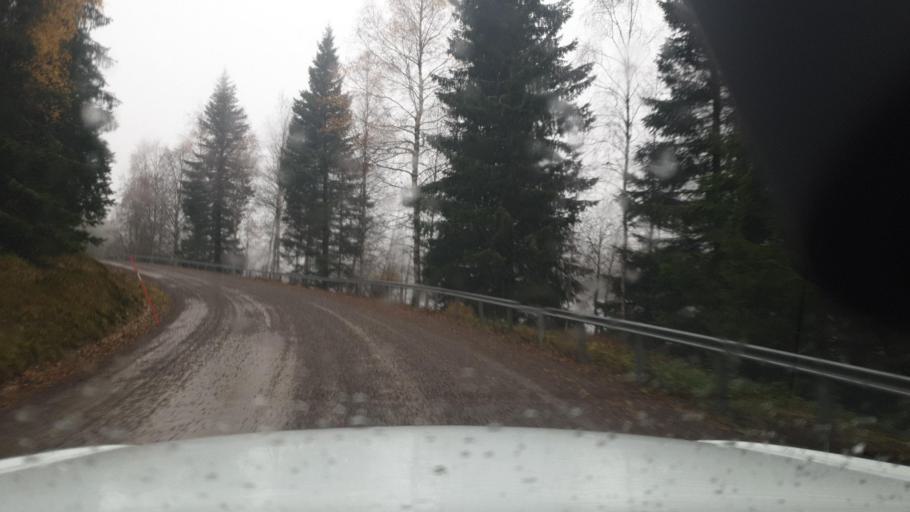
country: SE
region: Vaermland
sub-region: Sunne Kommun
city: Sunne
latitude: 59.8311
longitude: 12.9061
